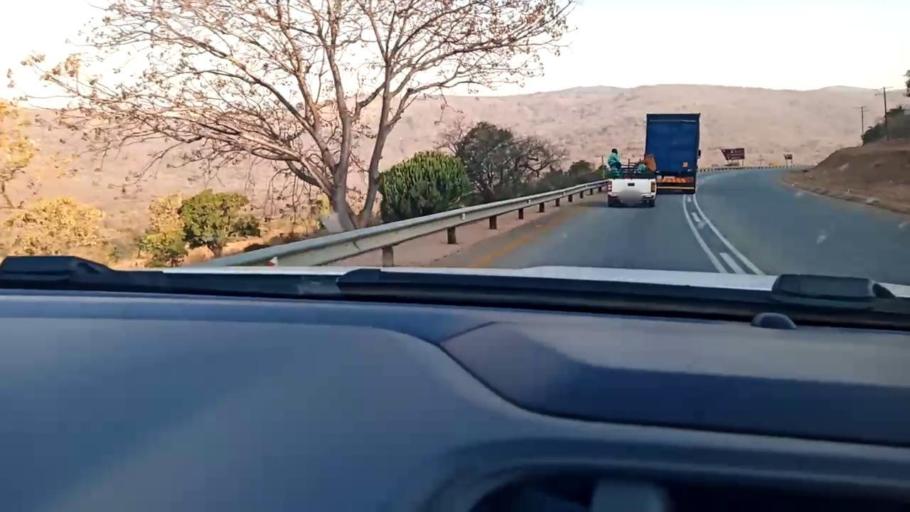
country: ZA
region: Limpopo
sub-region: Mopani District Municipality
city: Ga-Kgapane
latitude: -23.6495
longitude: 30.1719
